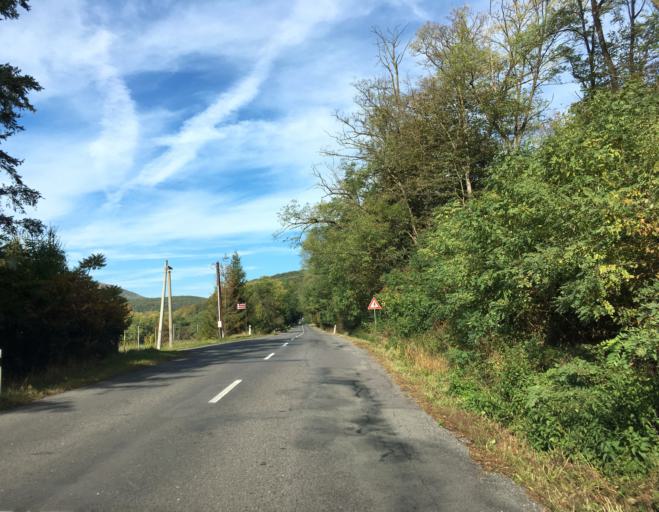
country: SK
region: Banskobystricky
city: Krupina
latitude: 48.2945
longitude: 18.9870
